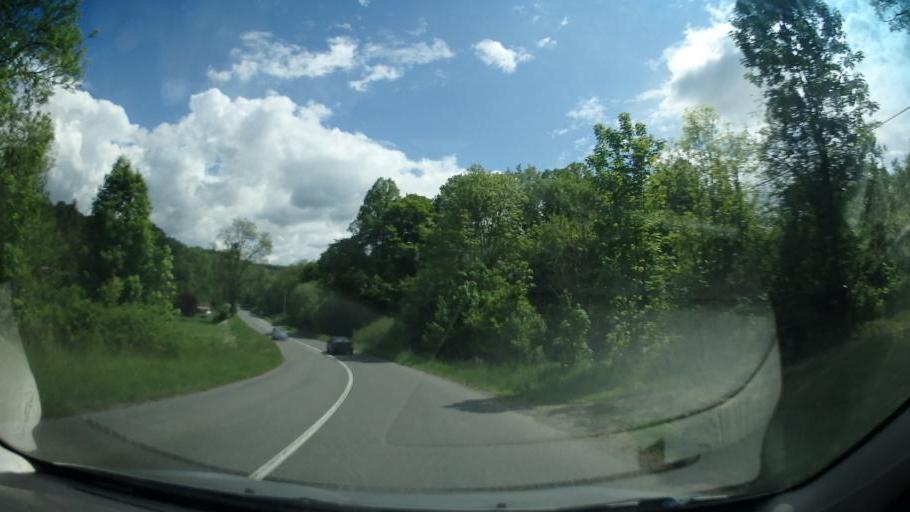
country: CZ
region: Pardubicky
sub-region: Okres Svitavy
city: Moravska Trebova
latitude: 49.7127
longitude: 16.6370
